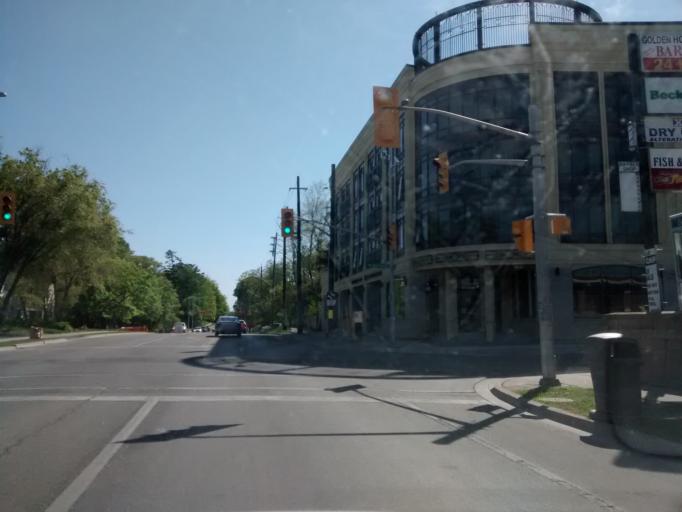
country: CA
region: Ontario
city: Oakville
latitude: 43.4369
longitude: -79.6778
